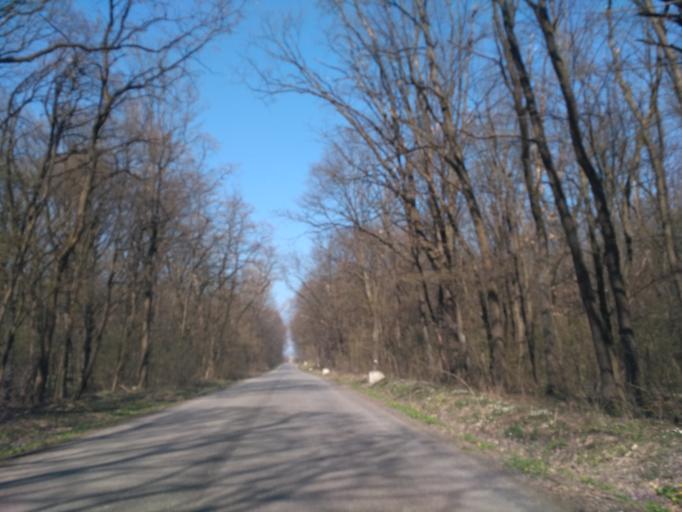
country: SK
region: Presovsky
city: Vranov nad Topl'ou
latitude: 48.7965
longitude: 21.6611
